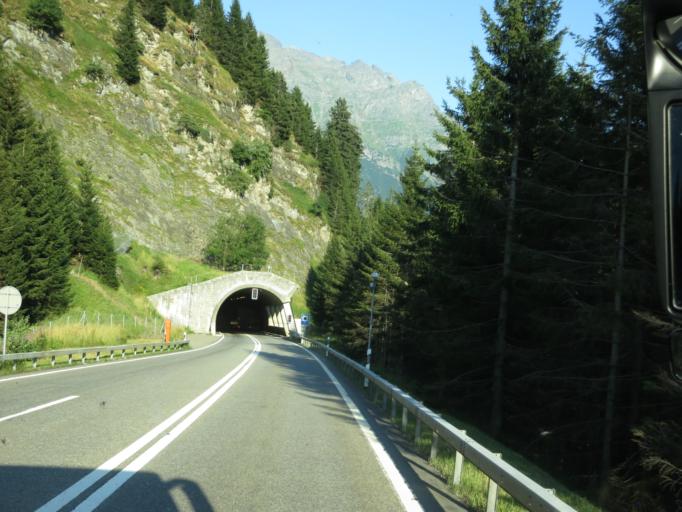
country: CH
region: Grisons
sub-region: Moesa District
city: Mesocco
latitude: 46.4333
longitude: 9.1997
